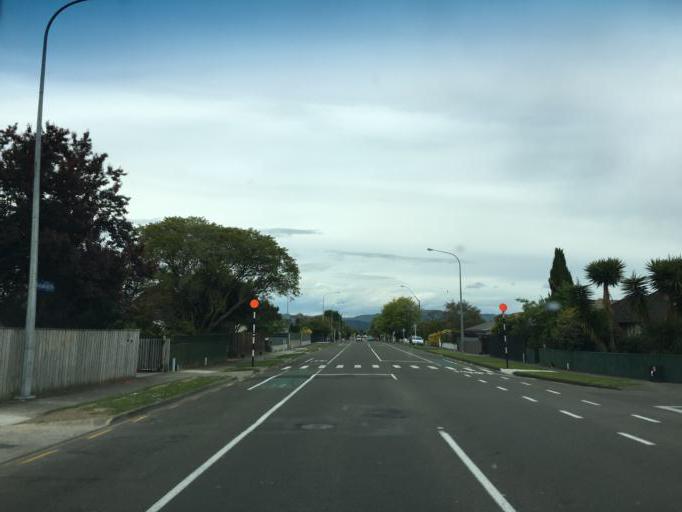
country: NZ
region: Manawatu-Wanganui
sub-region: Palmerston North City
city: Palmerston North
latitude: -40.3591
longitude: 175.5911
